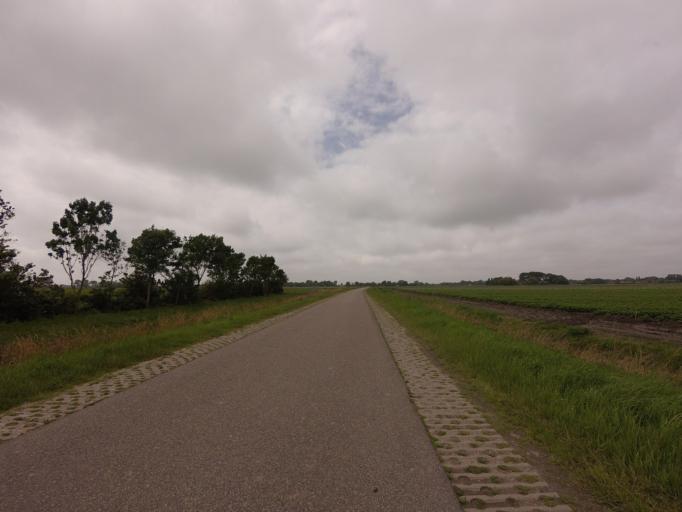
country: NL
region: North Holland
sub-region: Gemeente Schagen
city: Schagen
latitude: 52.7707
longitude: 4.7842
